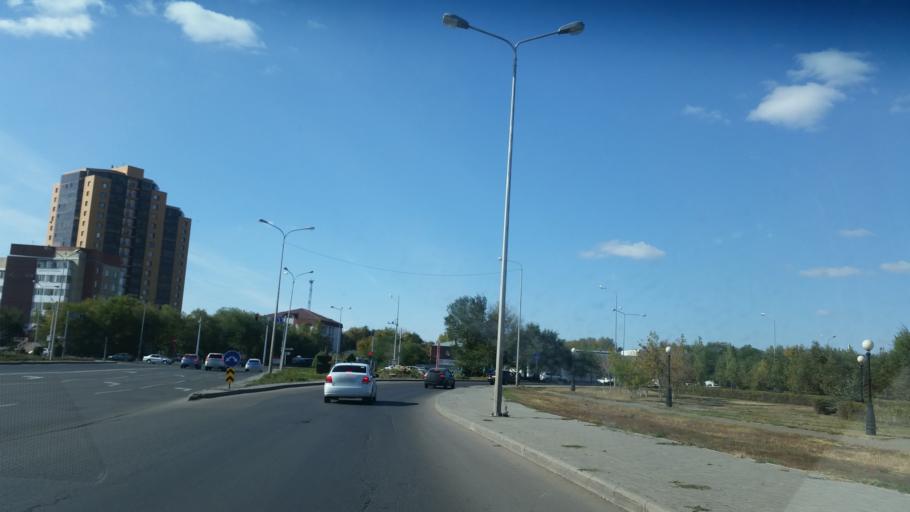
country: KZ
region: Astana Qalasy
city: Astana
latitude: 51.1649
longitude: 71.4768
